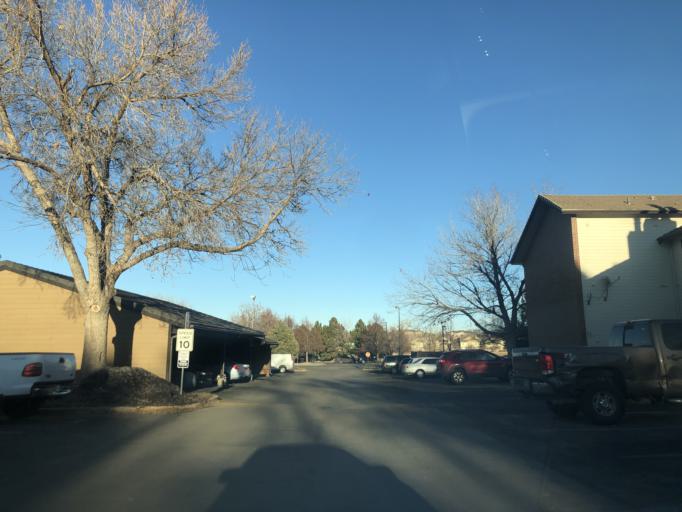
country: US
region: Colorado
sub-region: Adams County
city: Aurora
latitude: 39.7188
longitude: -104.8155
